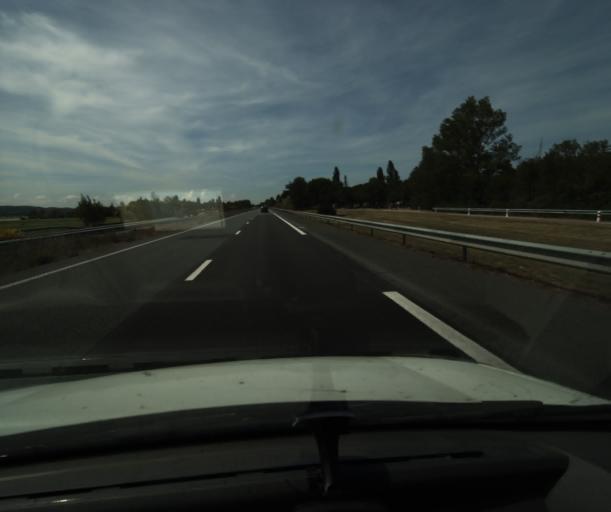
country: FR
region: Languedoc-Roussillon
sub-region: Departement de l'Aude
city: Saint-Martin-Lalande
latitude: 43.2753
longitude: 1.9948
